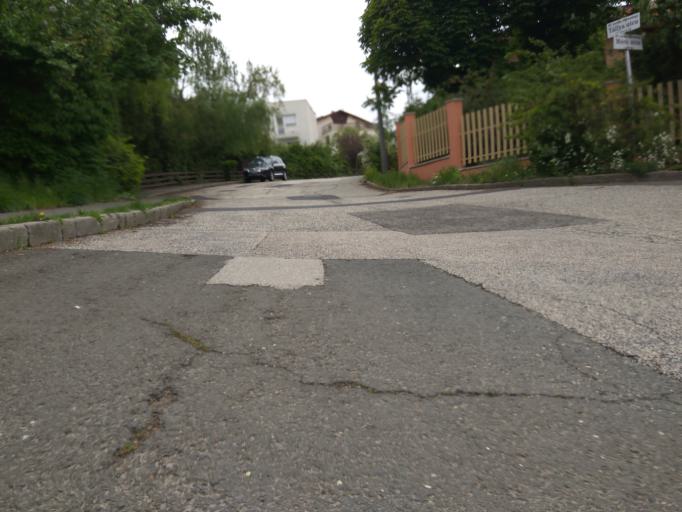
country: HU
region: Budapest
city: Budapest XII. keruelet
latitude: 47.4892
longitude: 18.9987
